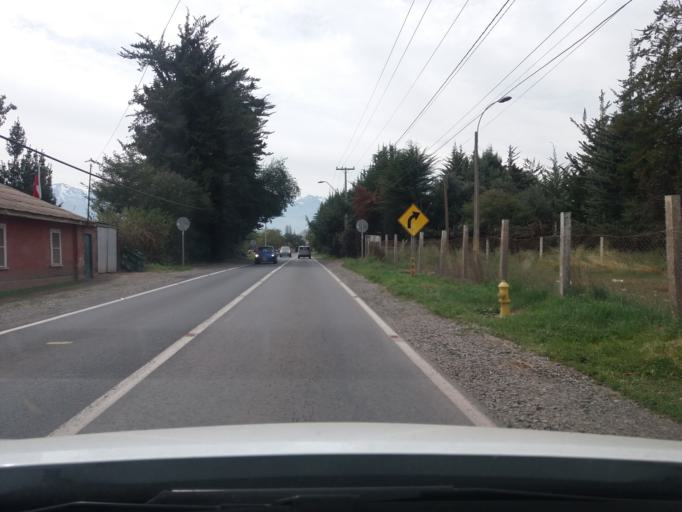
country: CL
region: Valparaiso
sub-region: Provincia de Los Andes
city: Los Andes
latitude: -32.8330
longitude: -70.6275
